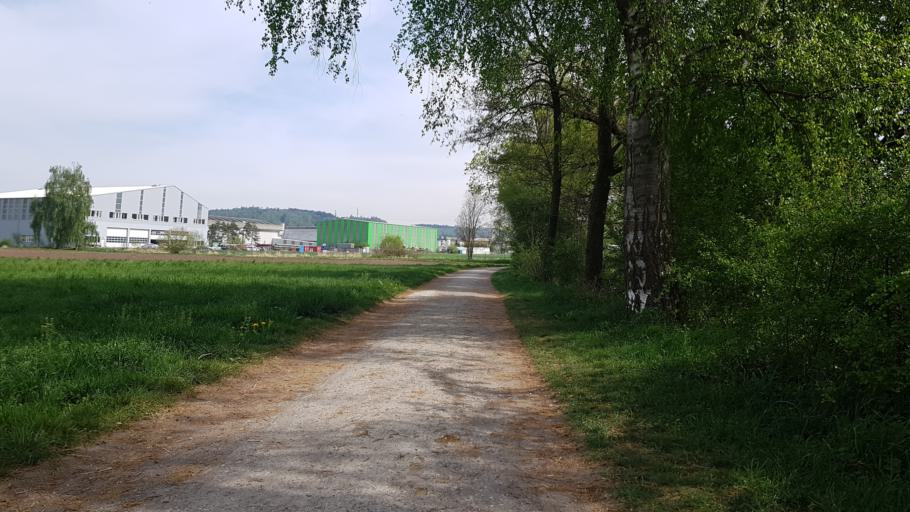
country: CH
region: Aargau
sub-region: Bezirk Kulm
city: Reinach
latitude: 47.2673
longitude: 8.1674
